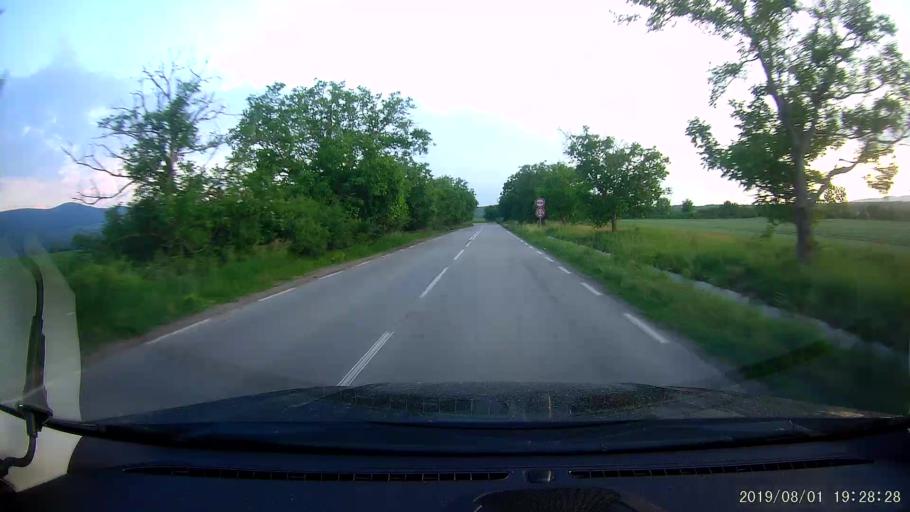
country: BG
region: Burgas
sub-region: Obshtina Sungurlare
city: Sungurlare
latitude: 42.8420
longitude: 26.9166
